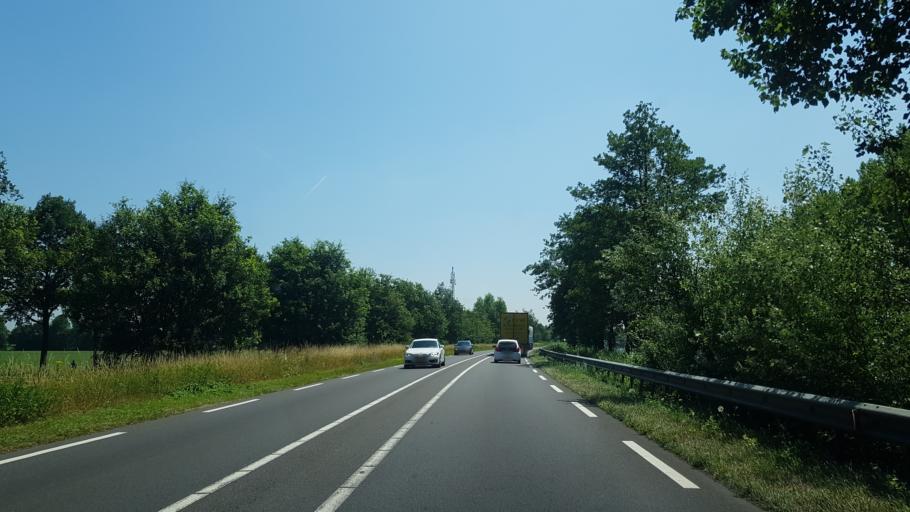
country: NL
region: North Brabant
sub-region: Gemeente Veghel
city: Keldonk
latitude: 51.5831
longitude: 5.5797
